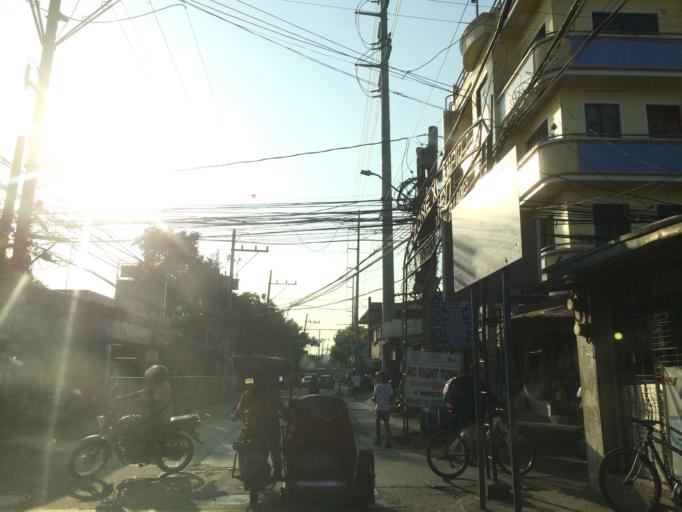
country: PH
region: Calabarzon
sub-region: Province of Rizal
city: San Mateo
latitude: 14.6814
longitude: 121.1177
